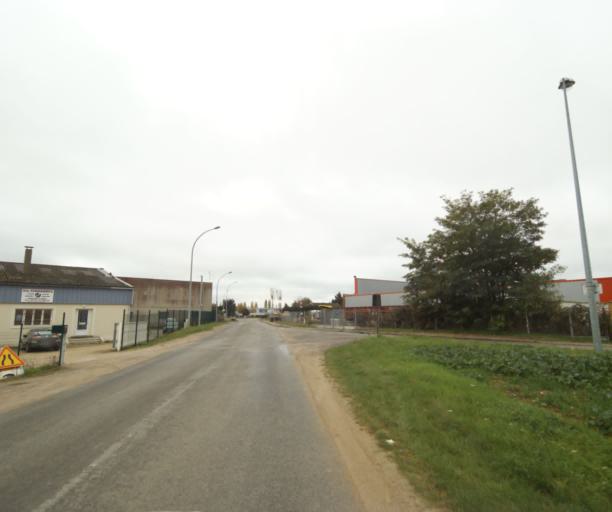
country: FR
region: Centre
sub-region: Departement d'Eure-et-Loir
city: Dreux
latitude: 48.7520
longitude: 1.3611
